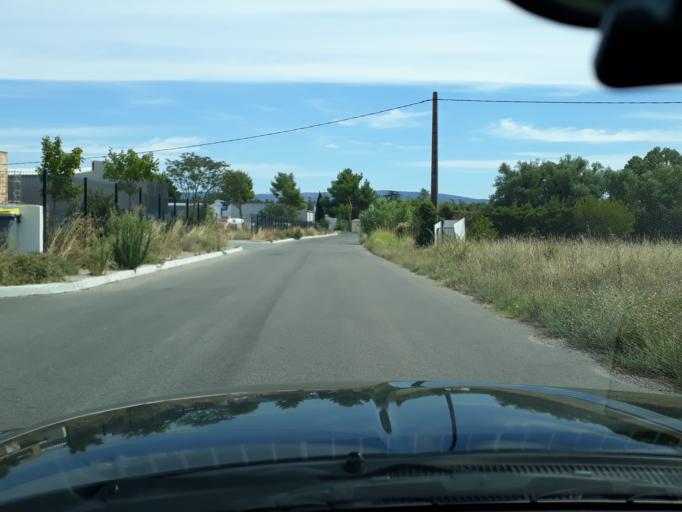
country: FR
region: Provence-Alpes-Cote d'Azur
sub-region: Departement du Vaucluse
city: Carpentras
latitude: 44.0382
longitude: 5.0469
